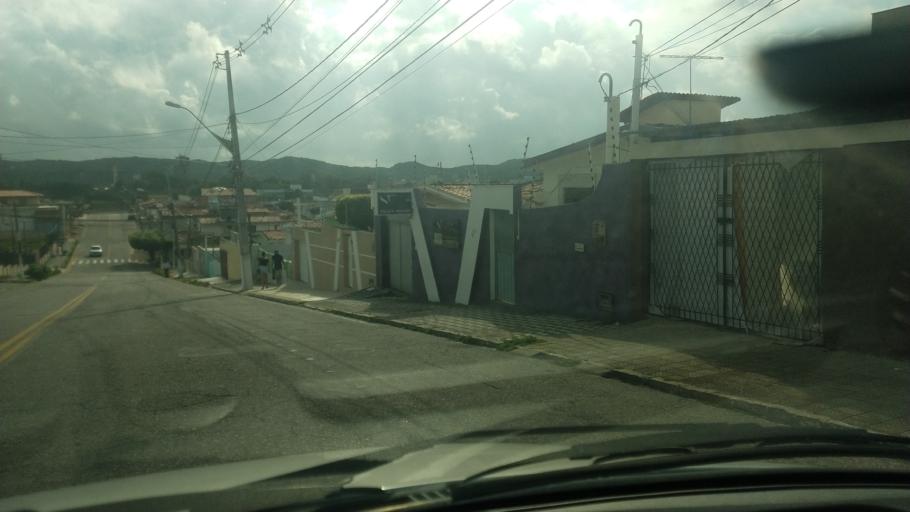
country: BR
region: Rio Grande do Norte
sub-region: Natal
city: Natal
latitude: -5.8429
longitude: -35.2070
